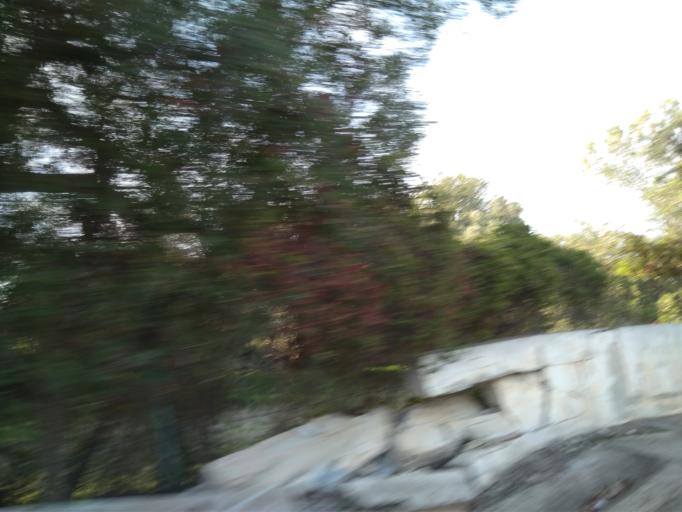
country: PT
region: Faro
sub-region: Faro
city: Santa Barbara de Nexe
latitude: 37.1015
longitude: -7.9617
